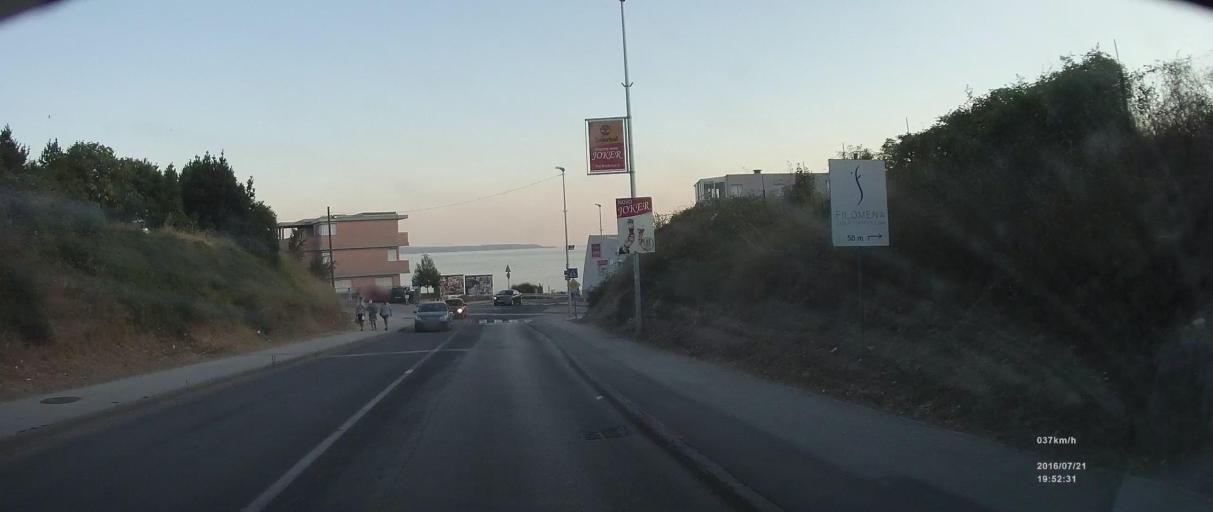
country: HR
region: Splitsko-Dalmatinska
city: Vranjic
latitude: 43.5047
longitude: 16.4779
